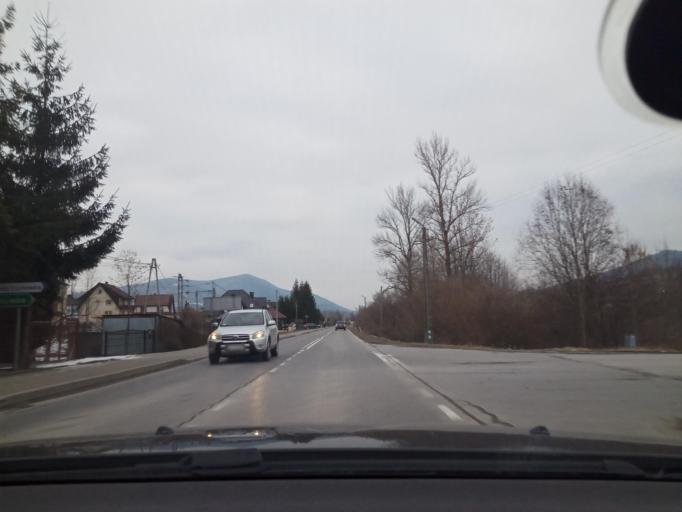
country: PL
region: Lesser Poland Voivodeship
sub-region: Powiat limanowski
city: Mszana Gorna
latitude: 49.6615
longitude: 20.0972
